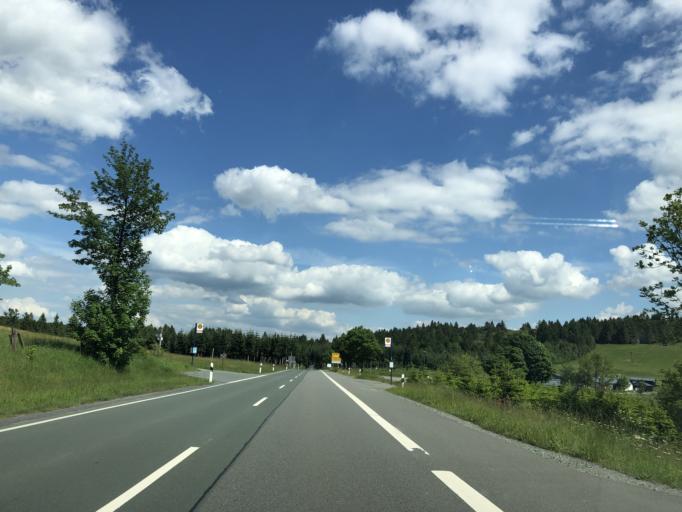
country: DE
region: North Rhine-Westphalia
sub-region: Regierungsbezirk Arnsberg
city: Winterberg
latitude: 51.1865
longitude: 8.4762
